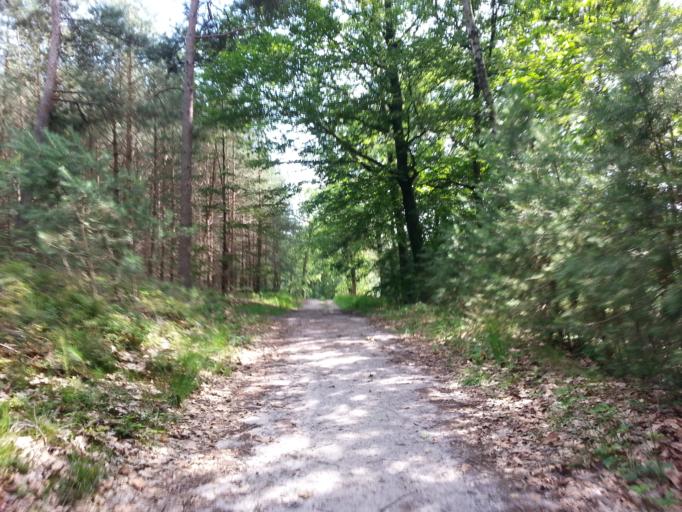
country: NL
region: Utrecht
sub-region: Gemeente Utrechtse Heuvelrug
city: Maarn
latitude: 52.0884
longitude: 5.3665
